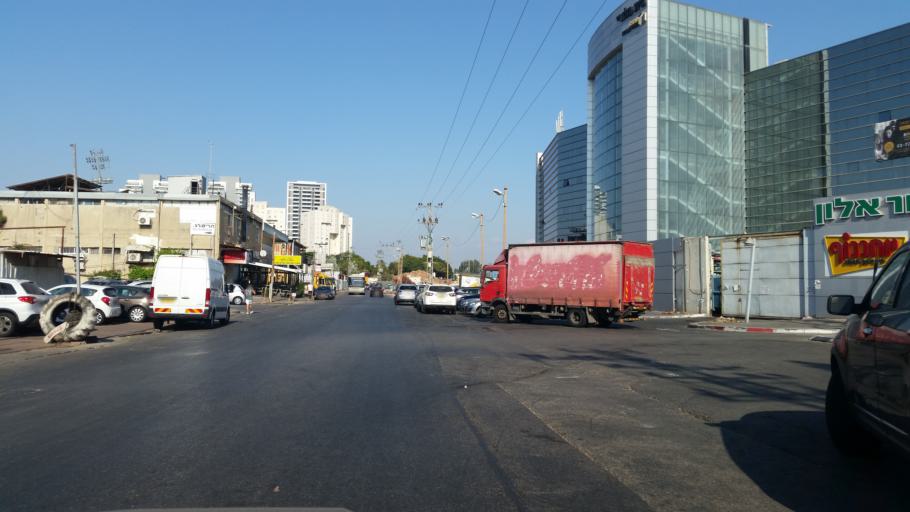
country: IL
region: Tel Aviv
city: Ramat HaSharon
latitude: 32.1288
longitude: 34.8580
